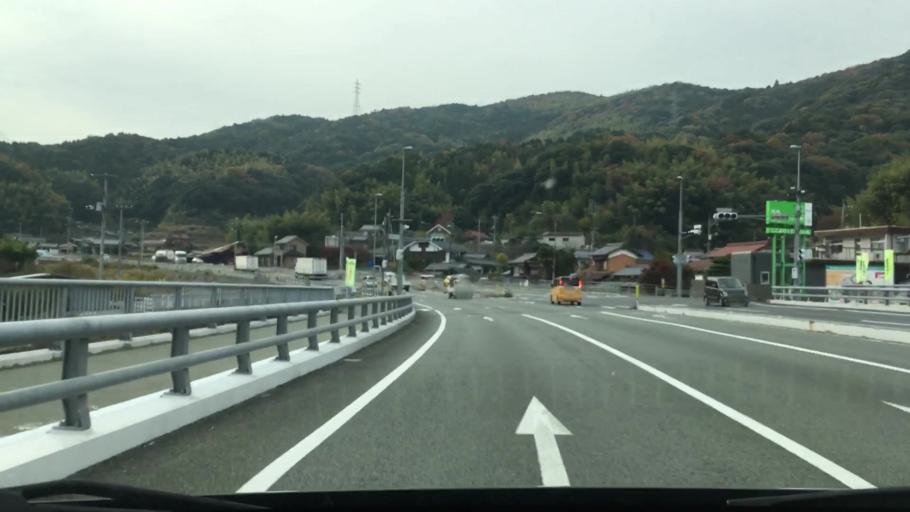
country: JP
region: Yamaguchi
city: Hofu
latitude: 34.0766
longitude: 131.6835
